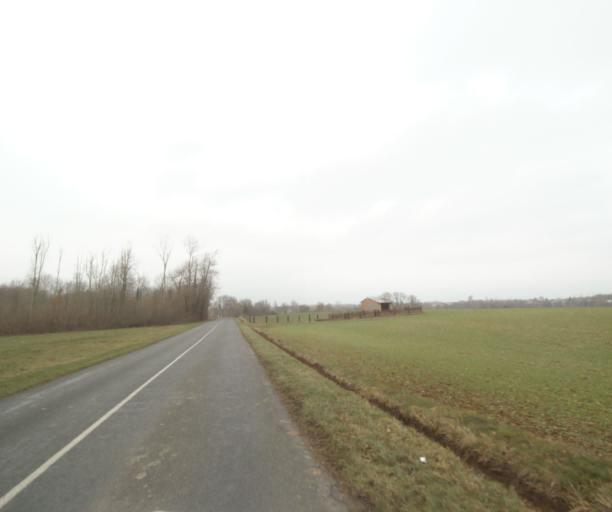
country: FR
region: Champagne-Ardenne
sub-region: Departement de la Marne
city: Pargny-sur-Saulx
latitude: 48.7386
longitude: 4.8563
